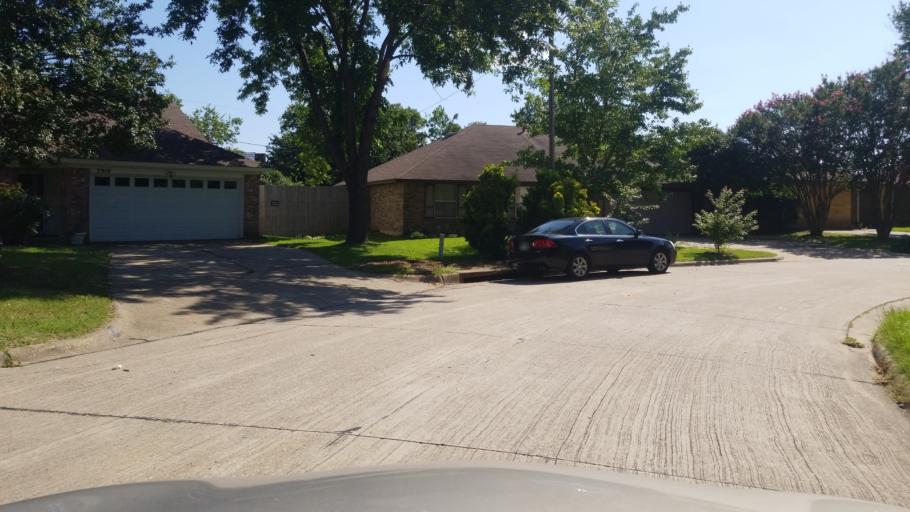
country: US
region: Texas
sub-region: Dallas County
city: Grand Prairie
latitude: 32.6785
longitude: -97.0160
